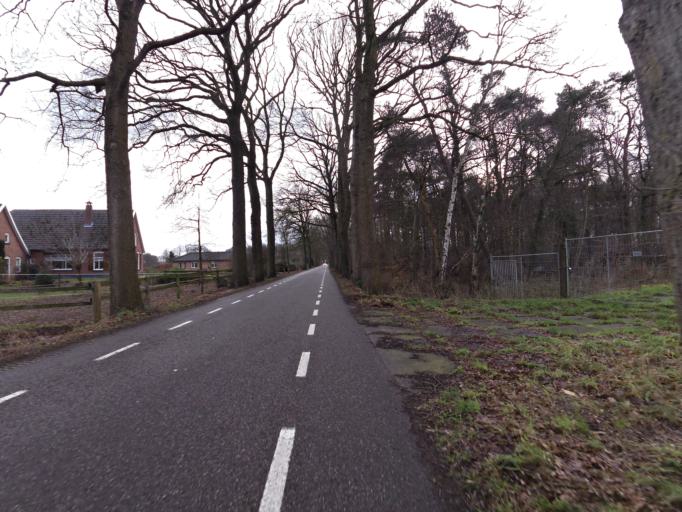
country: NL
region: Gelderland
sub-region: Oude IJsselstreek
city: Wisch
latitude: 51.9307
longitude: 6.4096
